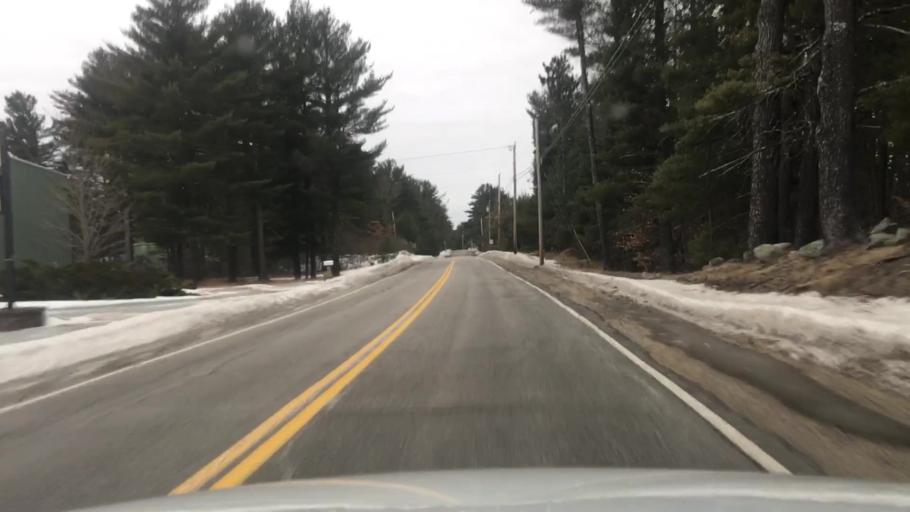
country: US
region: Maine
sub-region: York County
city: Shapleigh
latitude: 43.5624
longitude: -70.8576
